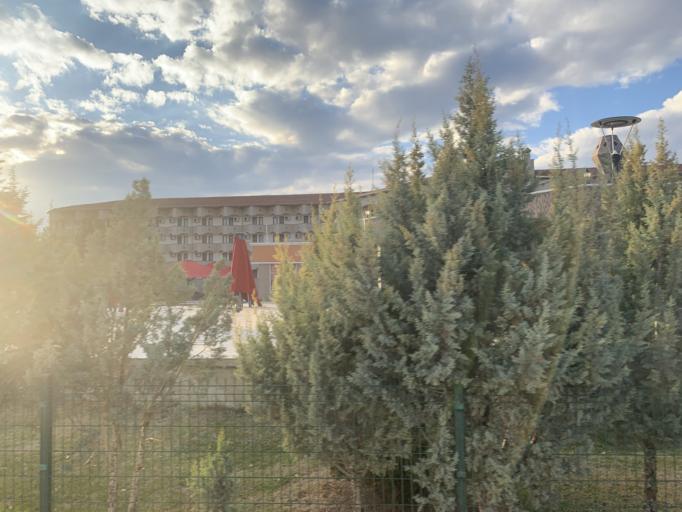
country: TR
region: Nevsehir
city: Avanos
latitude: 38.7026
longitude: 34.8387
